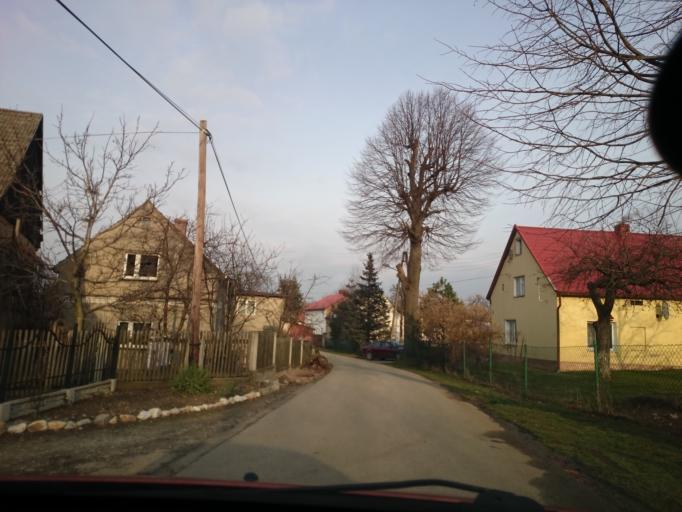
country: PL
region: Lower Silesian Voivodeship
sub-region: Powiat zabkowicki
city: Bardo
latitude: 50.5381
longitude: 16.7282
